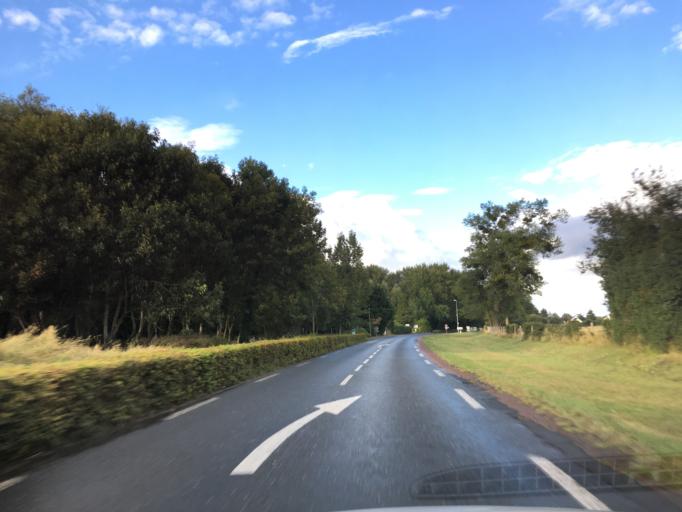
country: FR
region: Lower Normandy
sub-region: Departement du Calvados
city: Merville-Franceville-Plage
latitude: 49.2731
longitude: -0.2160
